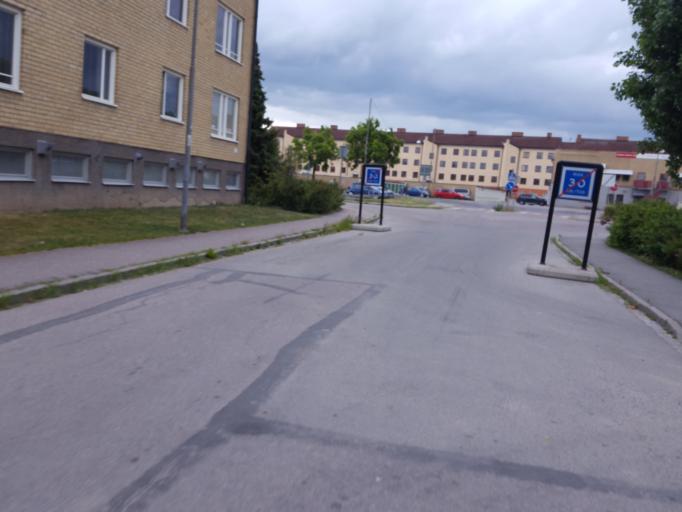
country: SE
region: Uppsala
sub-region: Uppsala Kommun
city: Uppsala
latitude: 59.8714
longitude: 17.6645
